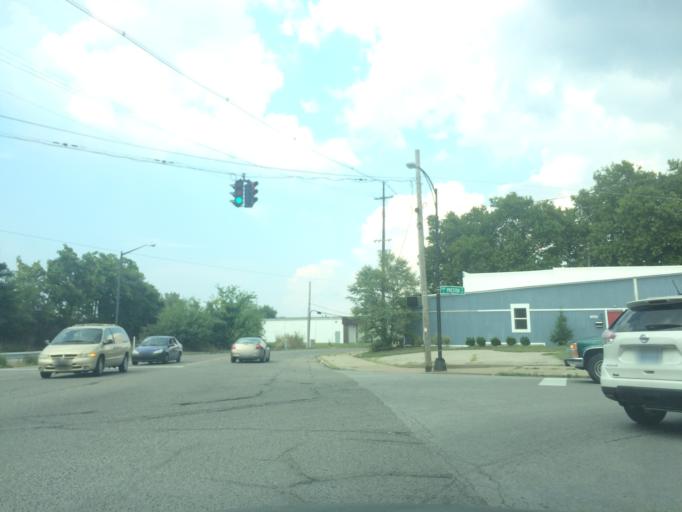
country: US
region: Kentucky
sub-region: Jefferson County
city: Louisville
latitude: 38.2258
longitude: -85.7511
